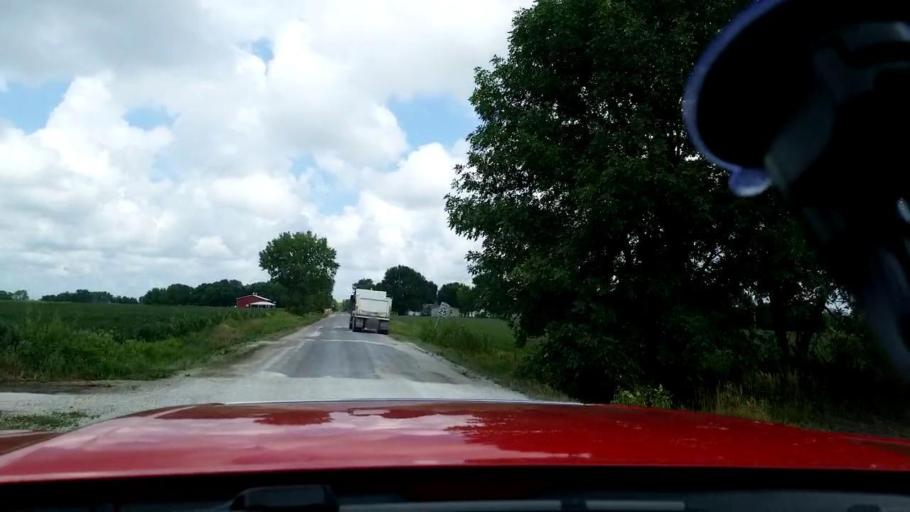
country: US
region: Iowa
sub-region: Decatur County
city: Lamoni
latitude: 40.7033
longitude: -94.0531
